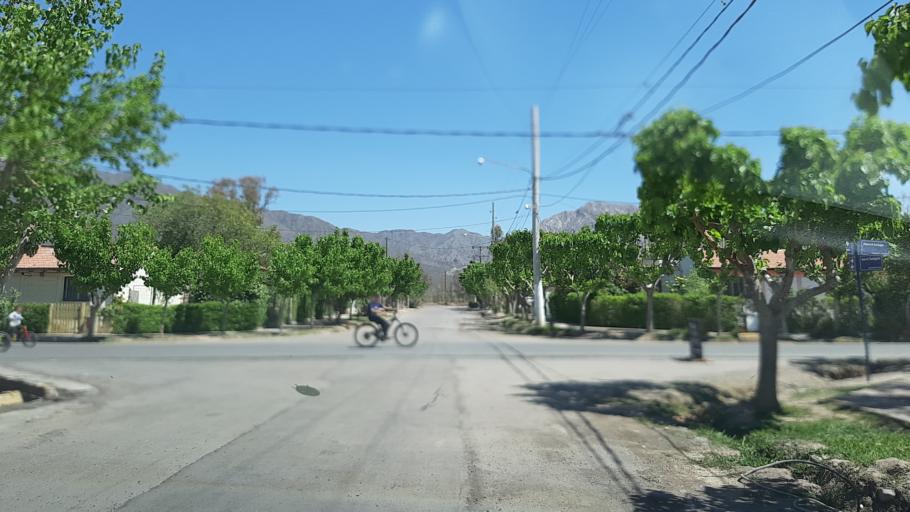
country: AR
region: San Juan
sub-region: Departamento de Zonda
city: Zonda
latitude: -31.5380
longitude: -68.7511
